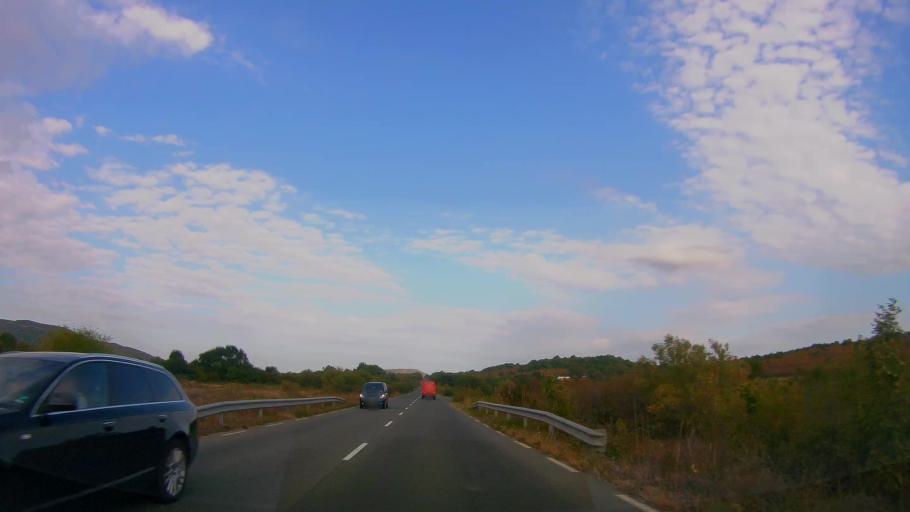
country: BG
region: Burgas
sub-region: Obshtina Sozopol
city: Sozopol
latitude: 42.3643
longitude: 27.6963
